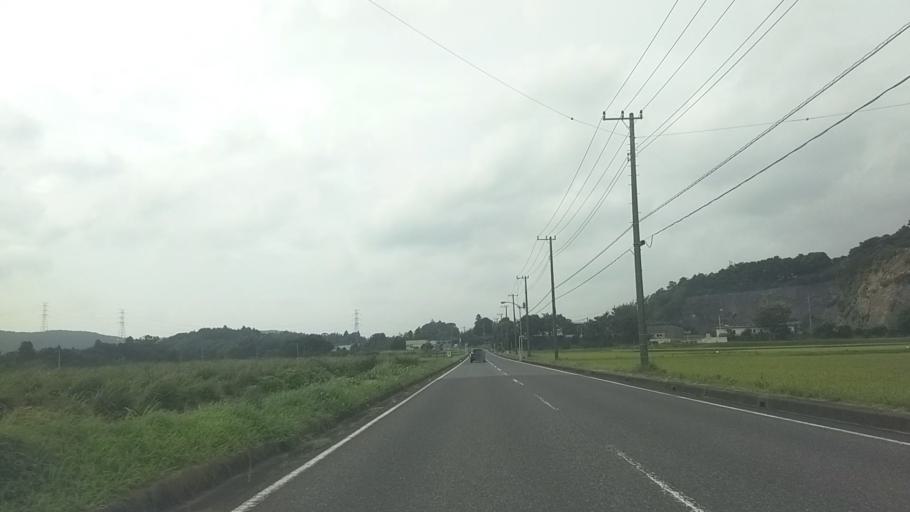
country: JP
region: Chiba
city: Kimitsu
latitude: 35.2739
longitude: 139.9955
